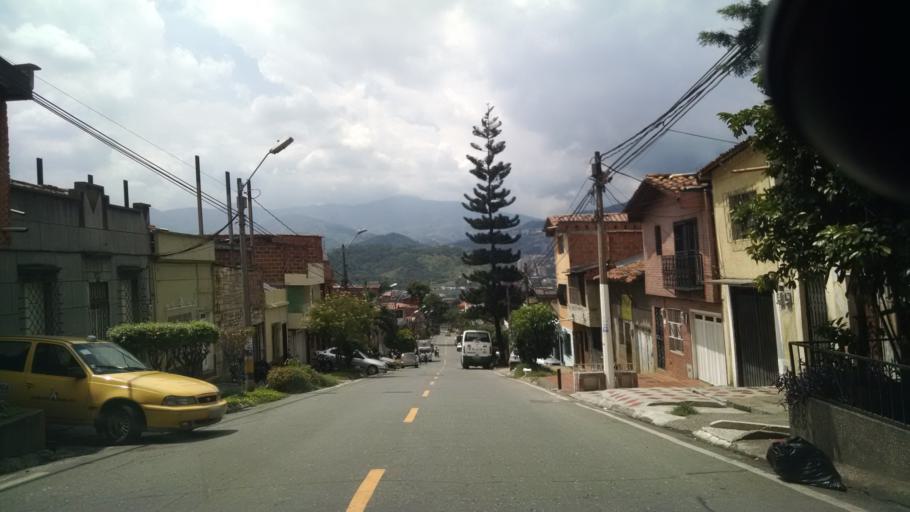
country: CO
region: Antioquia
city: Medellin
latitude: 6.2649
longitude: -75.5574
